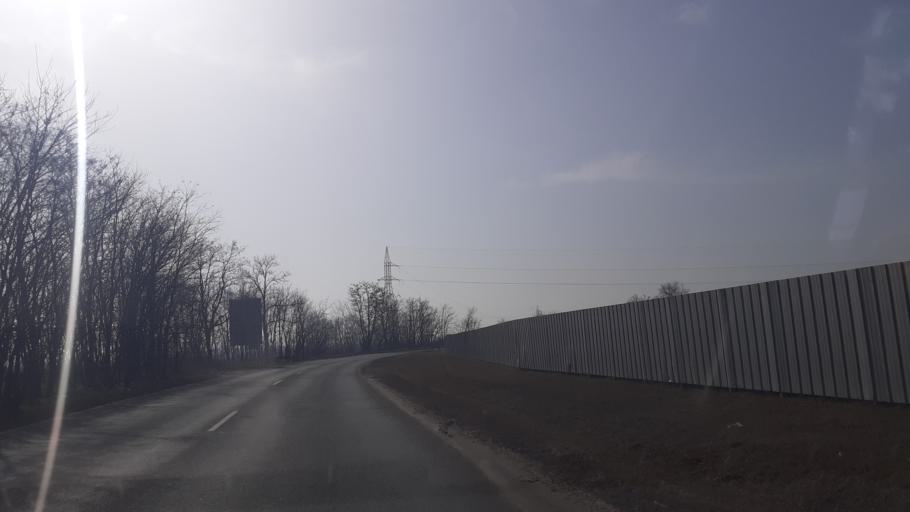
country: HU
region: Pest
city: Orkeny
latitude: 47.1455
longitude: 19.4602
